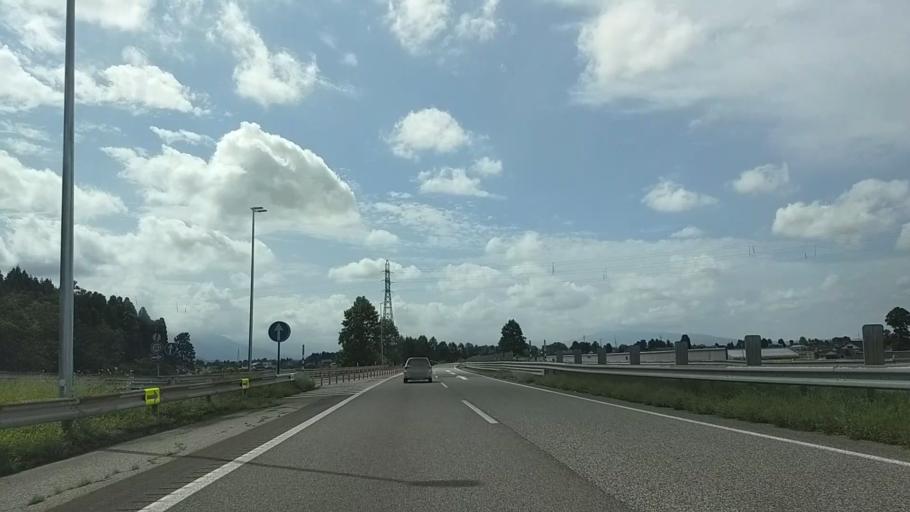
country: JP
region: Toyama
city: Takaoka
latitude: 36.6694
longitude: 137.0306
